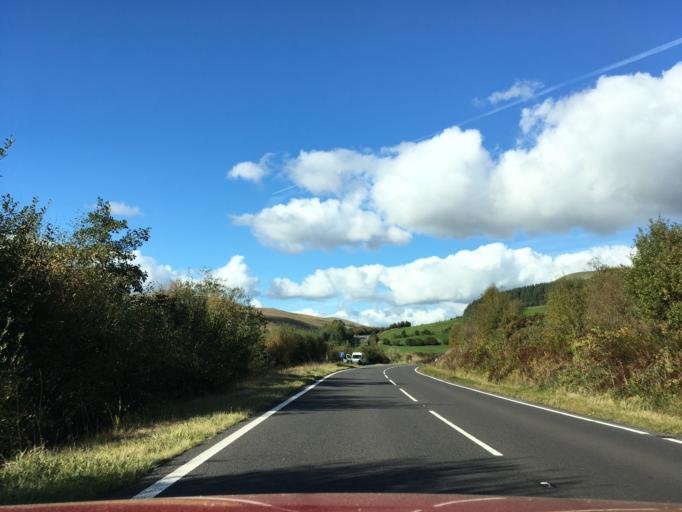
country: GB
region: Wales
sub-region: Rhondda Cynon Taf
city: Hirwaun
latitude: 51.8338
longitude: -3.4604
